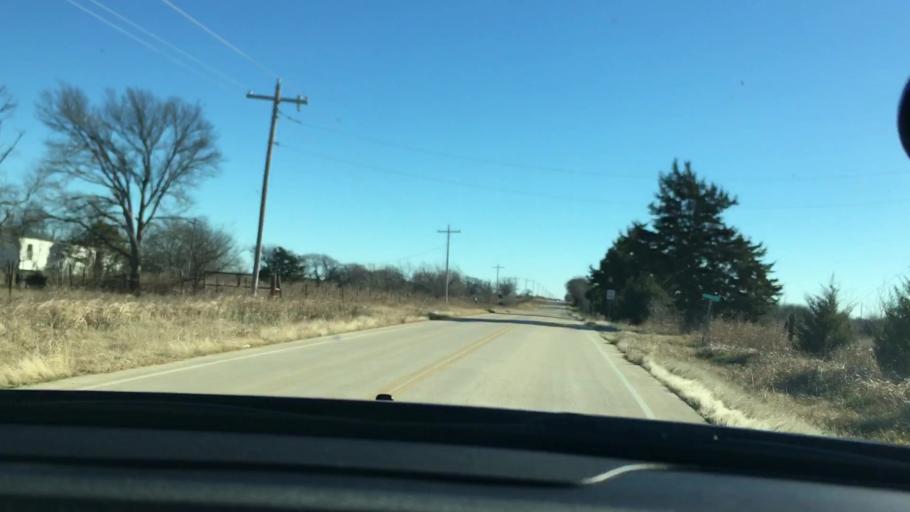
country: US
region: Oklahoma
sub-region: Marshall County
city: Madill
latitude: 34.1144
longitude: -96.6715
